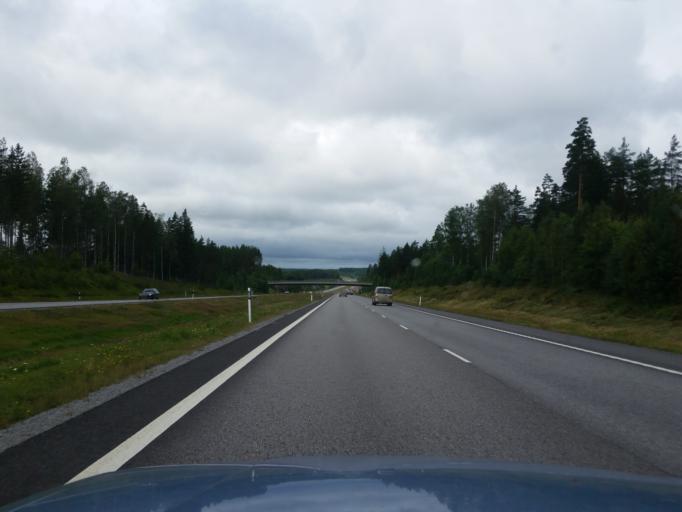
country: FI
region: Varsinais-Suomi
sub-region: Loimaa
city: Marttila
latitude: 60.4284
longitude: 22.8794
